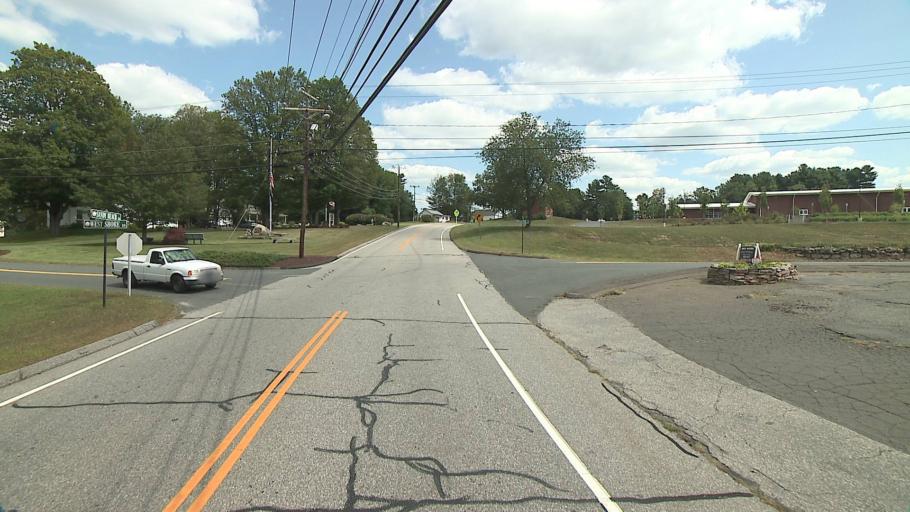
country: US
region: Connecticut
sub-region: Tolland County
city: Crystal Lake
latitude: 41.9312
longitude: -72.3805
